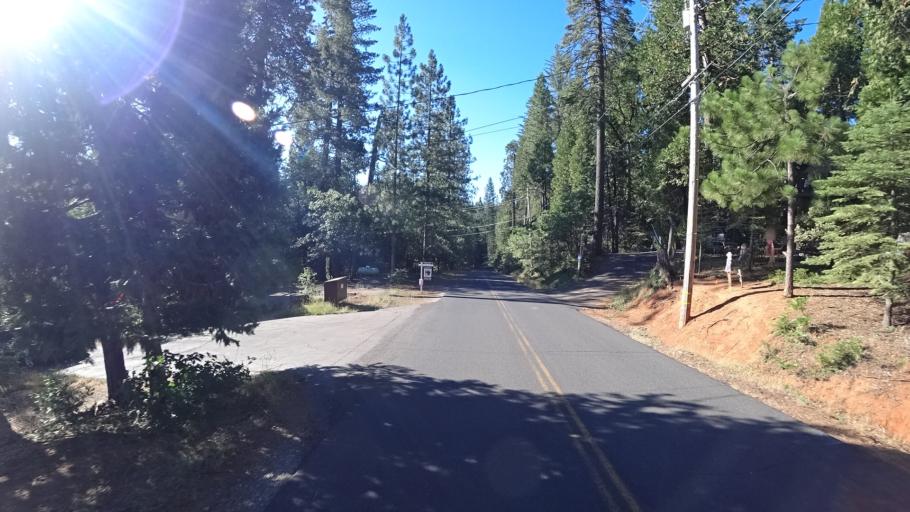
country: US
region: California
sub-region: Calaveras County
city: Arnold
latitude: 38.2590
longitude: -120.3310
